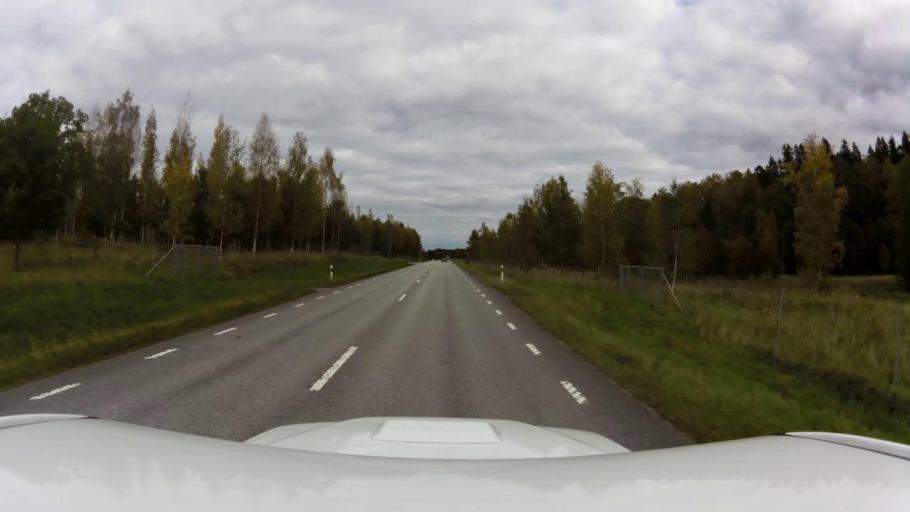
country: SE
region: OEstergoetland
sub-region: Kinda Kommun
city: Rimforsa
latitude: 58.2040
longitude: 15.6685
